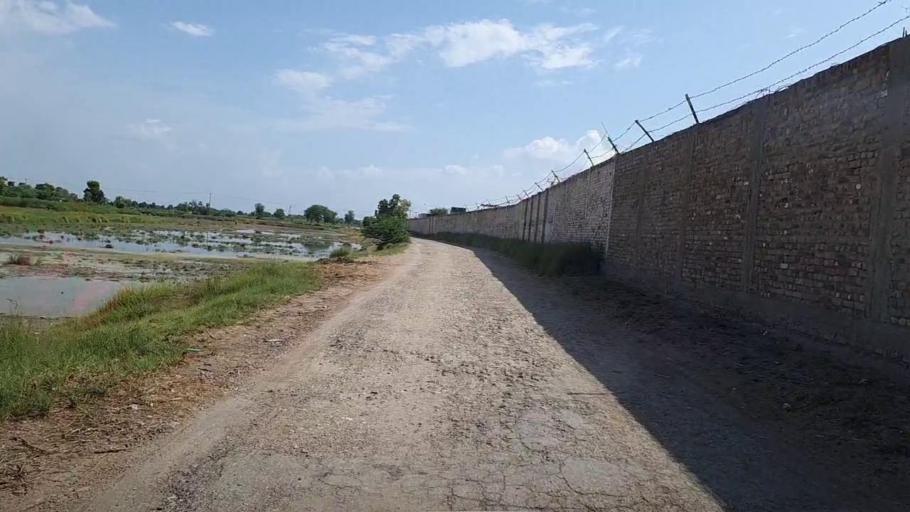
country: PK
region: Sindh
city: Bhiria
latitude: 26.9003
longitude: 68.2262
